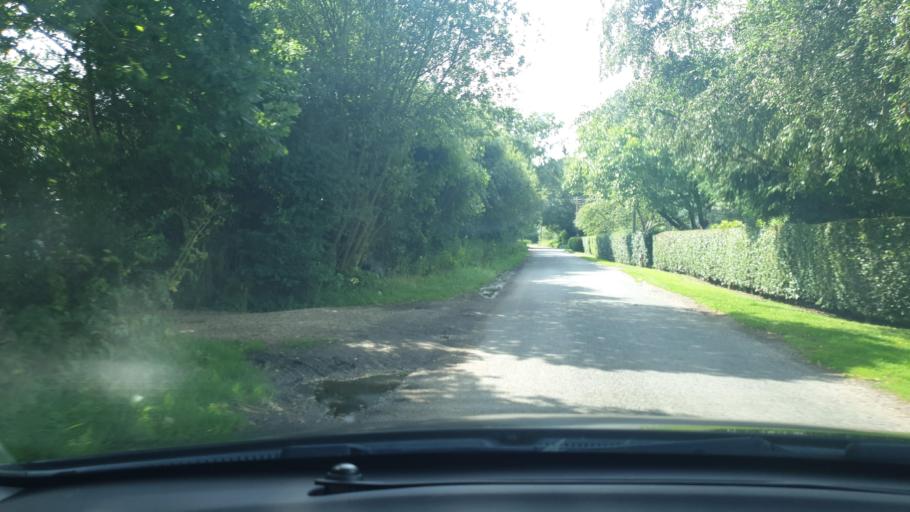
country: GB
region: England
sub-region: Essex
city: Alresford
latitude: 51.9142
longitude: 1.0063
